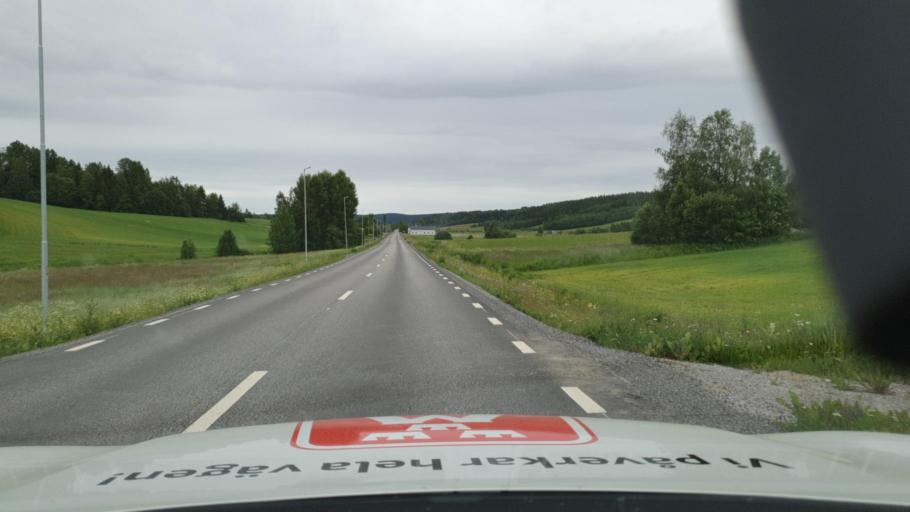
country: SE
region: Vaesterbotten
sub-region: Vannas Kommun
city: Vaennaes
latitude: 63.7655
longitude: 19.6242
